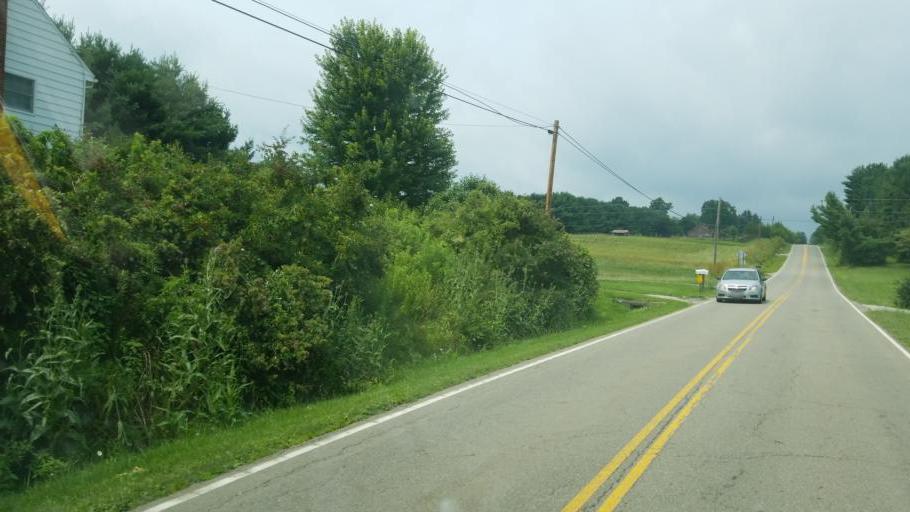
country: US
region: Ohio
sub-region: Licking County
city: Granville
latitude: 40.1454
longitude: -82.4799
